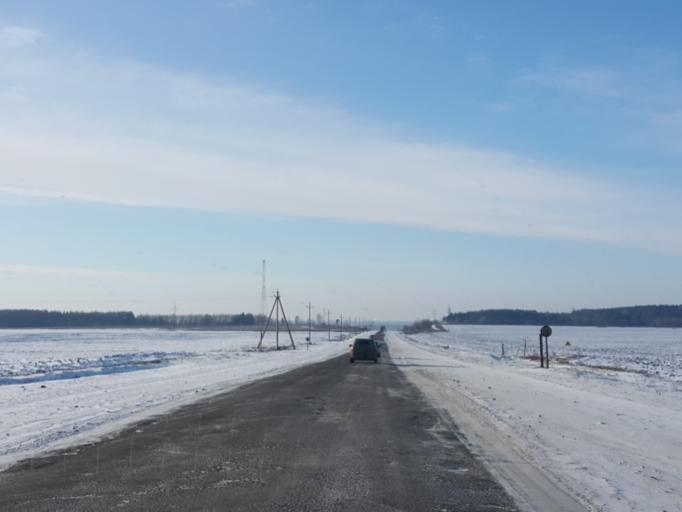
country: RU
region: Tambov
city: Znamenka
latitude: 52.4235
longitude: 41.5021
